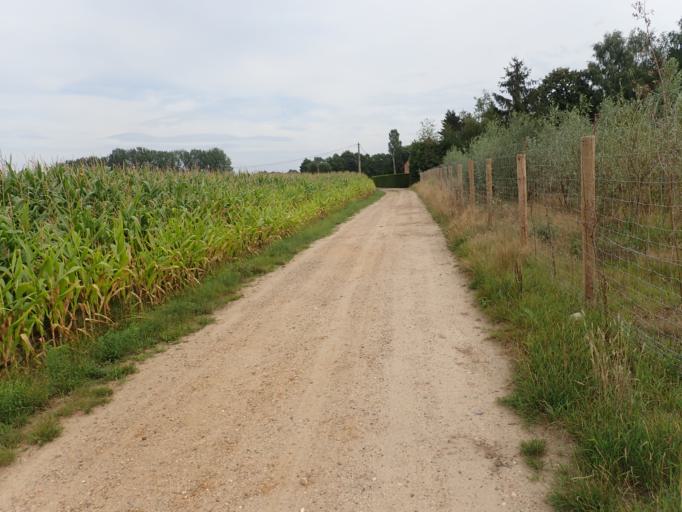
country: BE
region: Flanders
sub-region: Provincie Antwerpen
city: Ranst
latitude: 51.2102
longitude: 4.5635
